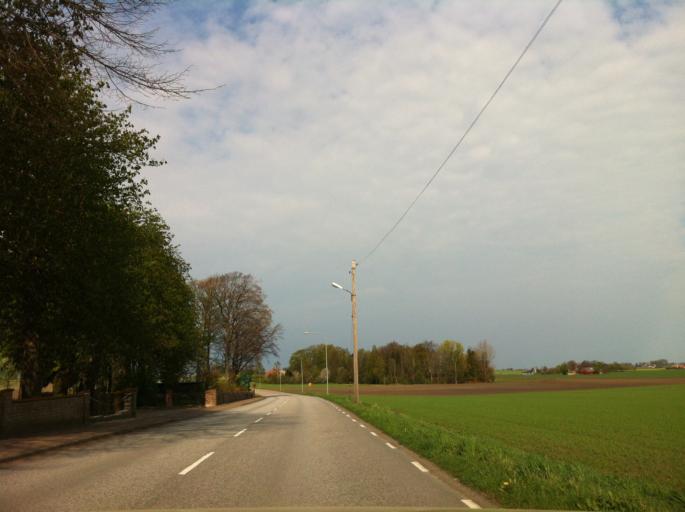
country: SE
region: Skane
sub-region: Helsingborg
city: Glumslov
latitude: 55.9351
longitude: 12.8663
